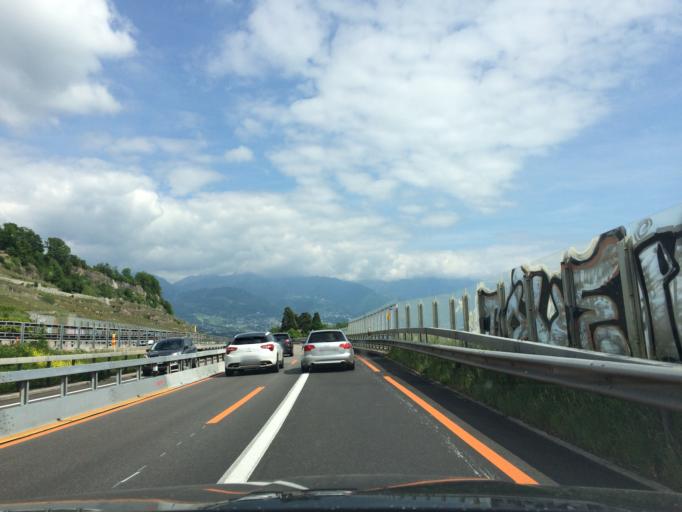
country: CH
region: Vaud
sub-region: Lavaux-Oron District
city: Chexbres
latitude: 46.4771
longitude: 6.7978
